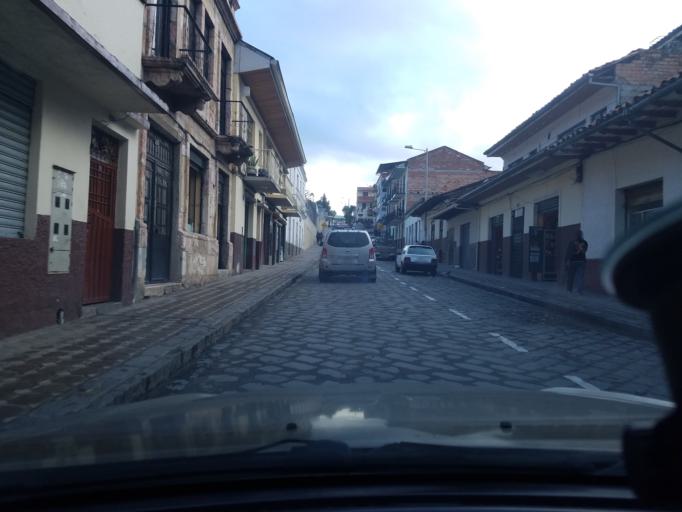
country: EC
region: Azuay
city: Cuenca
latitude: -2.8923
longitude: -79.0010
